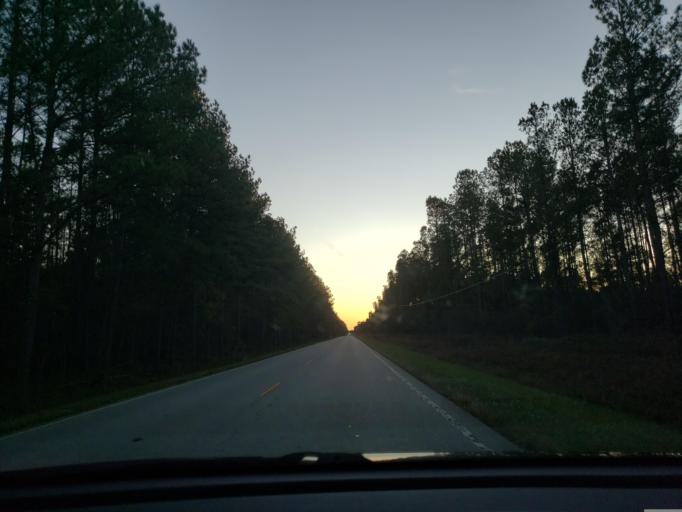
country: US
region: North Carolina
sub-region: Onslow County
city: Half Moon
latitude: 34.7266
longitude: -77.6031
